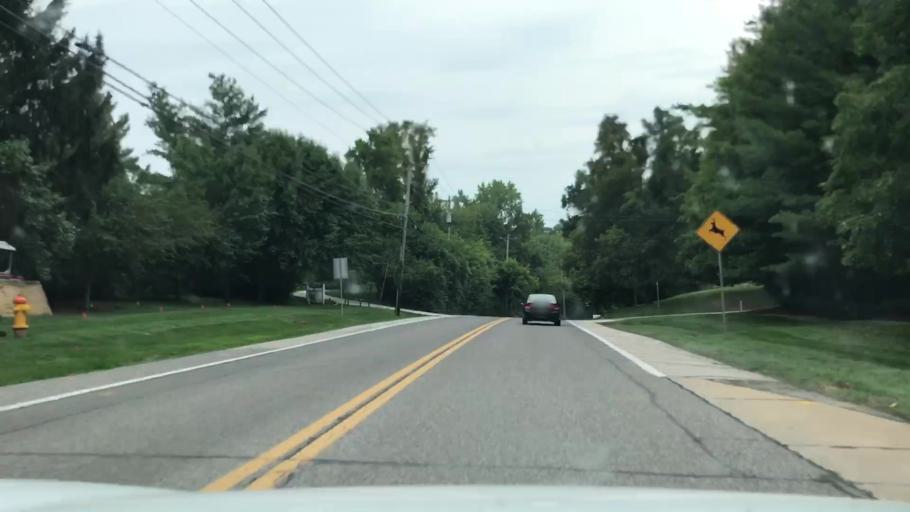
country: US
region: Missouri
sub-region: Saint Louis County
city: Chesterfield
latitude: 38.6554
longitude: -90.5890
